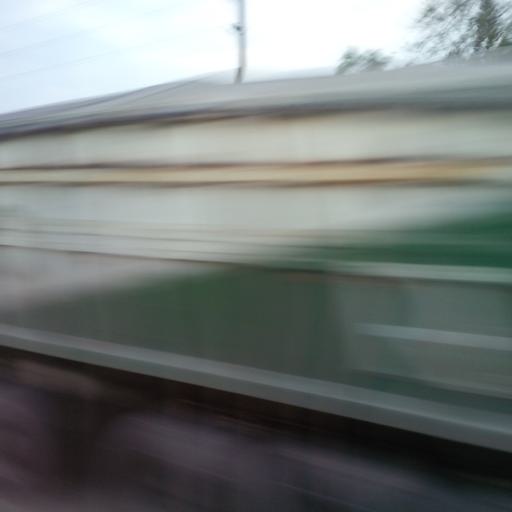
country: EC
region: Canar
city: La Troncal
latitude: -2.3368
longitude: -79.3931
